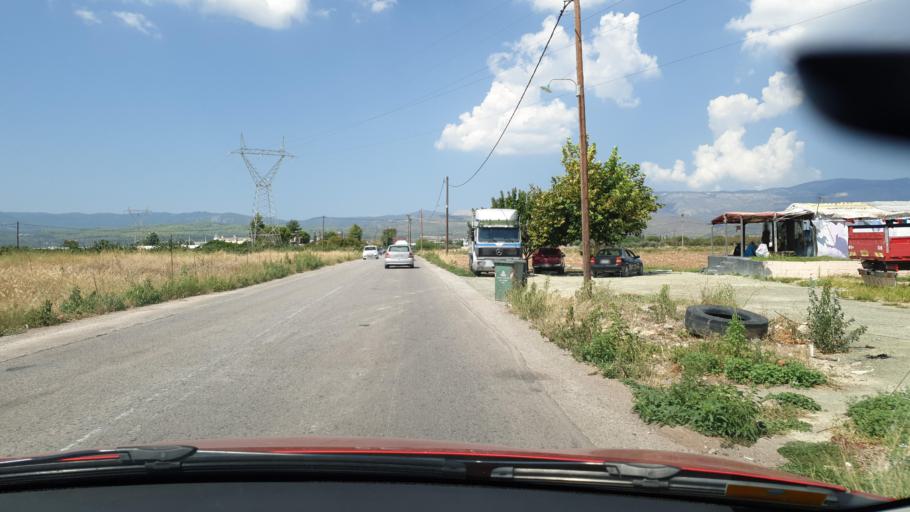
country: GR
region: Central Greece
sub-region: Nomos Evvoias
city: Kastella
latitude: 38.5596
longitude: 23.6324
